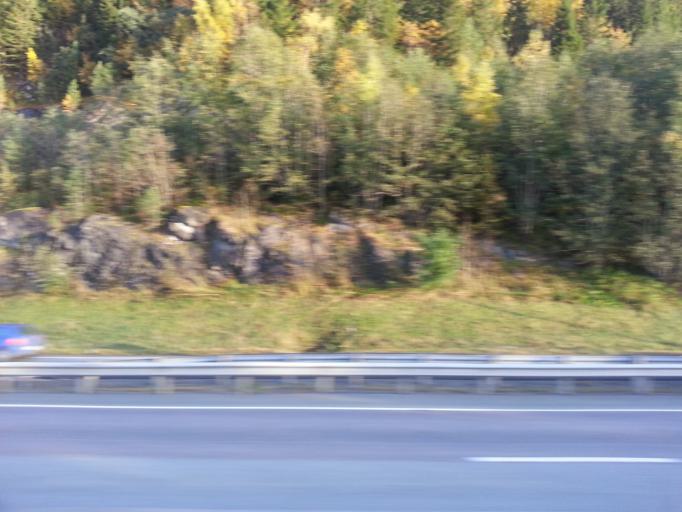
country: NO
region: Sor-Trondelag
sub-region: Malvik
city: Hommelvik
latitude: 63.4113
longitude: 10.8170
